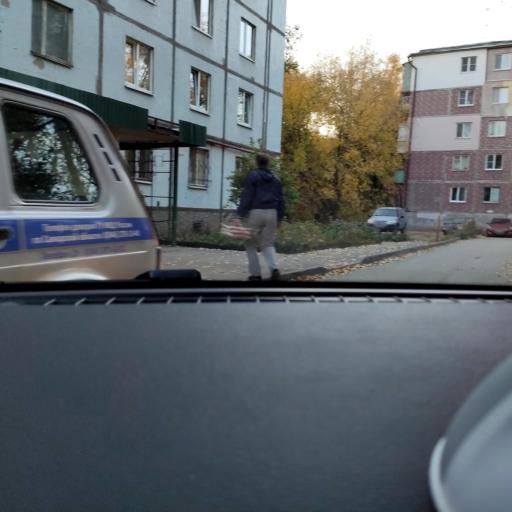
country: RU
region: Samara
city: Samara
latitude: 53.2418
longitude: 50.2466
